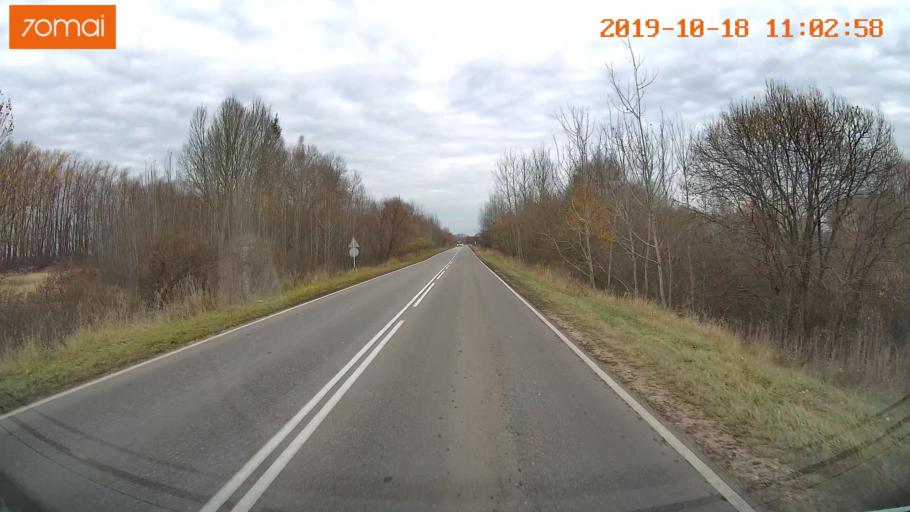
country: RU
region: Tula
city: Yepifan'
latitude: 53.8730
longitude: 38.5449
